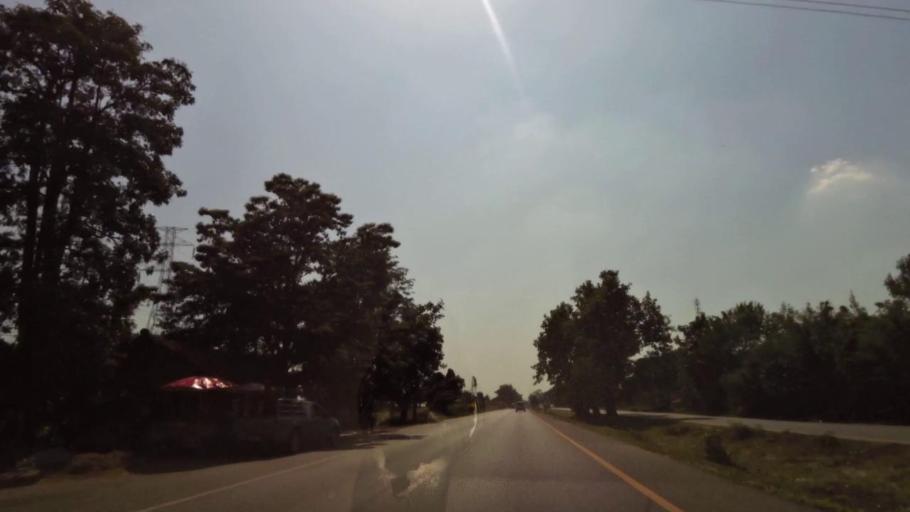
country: TH
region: Phichit
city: Wachira Barami
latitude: 16.3899
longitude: 100.1386
